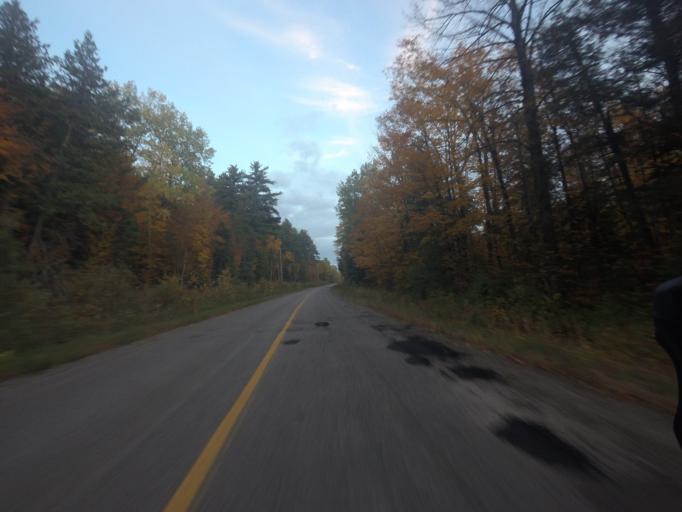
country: CA
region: Ontario
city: Renfrew
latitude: 45.3547
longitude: -76.9539
